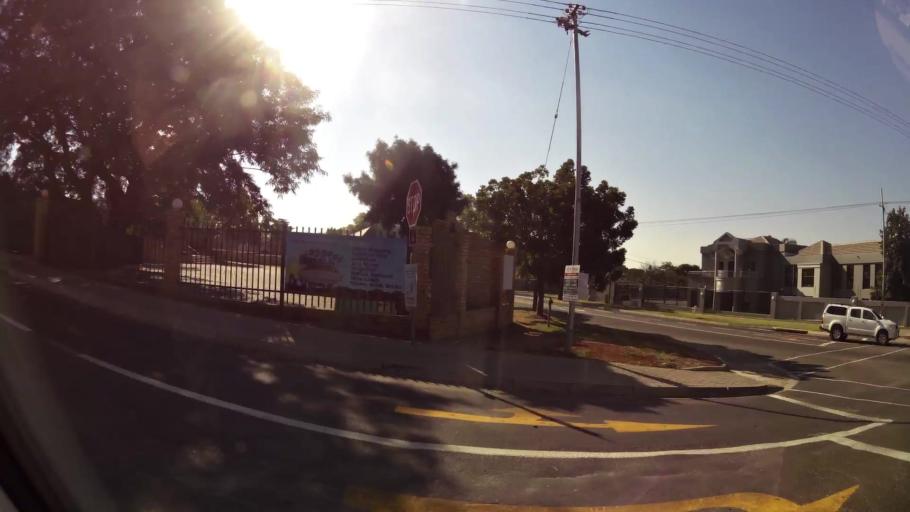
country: ZA
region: Gauteng
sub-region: City of Tshwane Metropolitan Municipality
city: Pretoria
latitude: -25.7870
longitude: 28.2614
